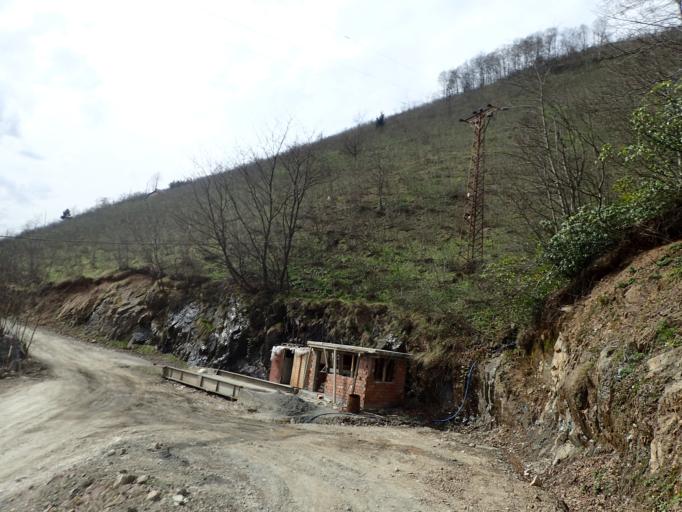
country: TR
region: Ordu
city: Kabaduz
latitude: 40.8141
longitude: 37.8924
